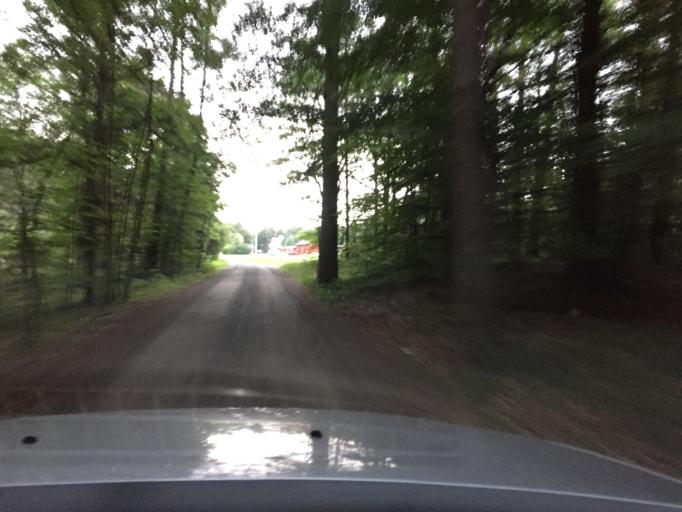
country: SE
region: Skane
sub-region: Kristianstads Kommun
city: Degeberga
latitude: 55.7323
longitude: 14.1245
